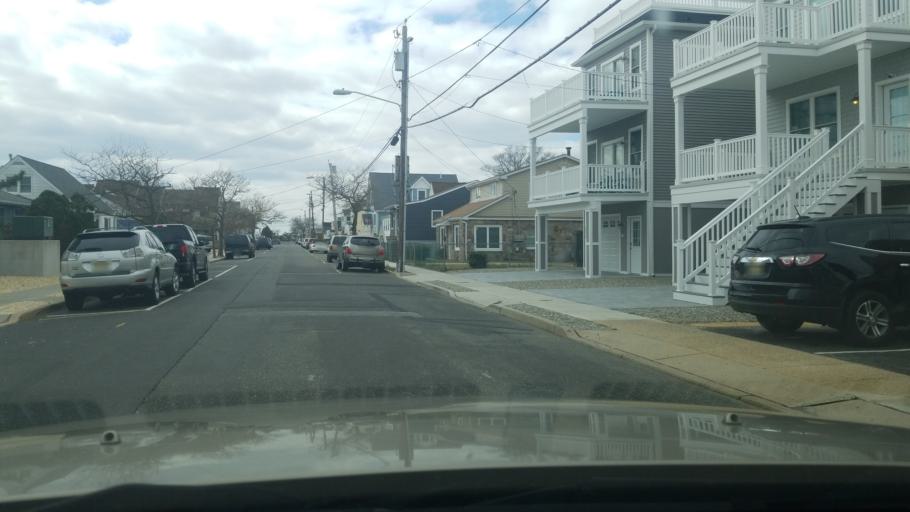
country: US
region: New Jersey
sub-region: Ocean County
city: Seaside Heights
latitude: 39.9456
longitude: -74.0749
